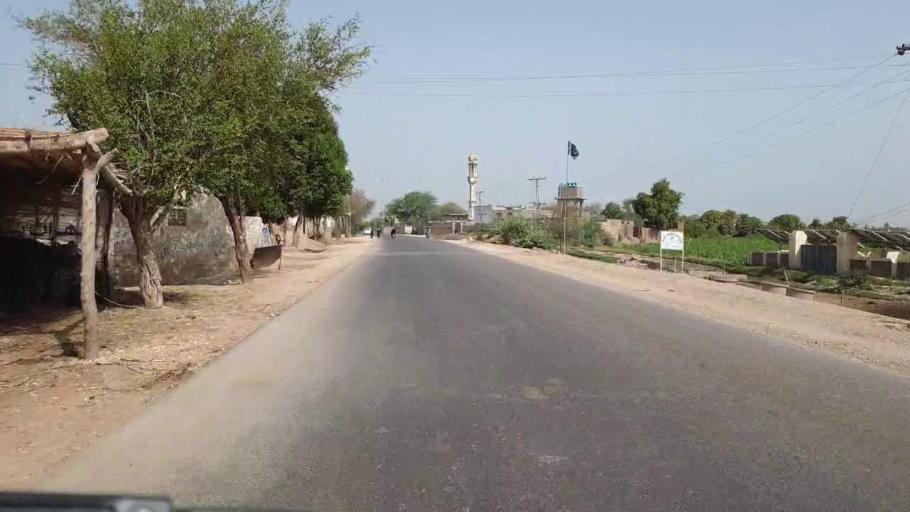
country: PK
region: Sindh
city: Sakrand
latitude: 26.2772
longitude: 68.1477
